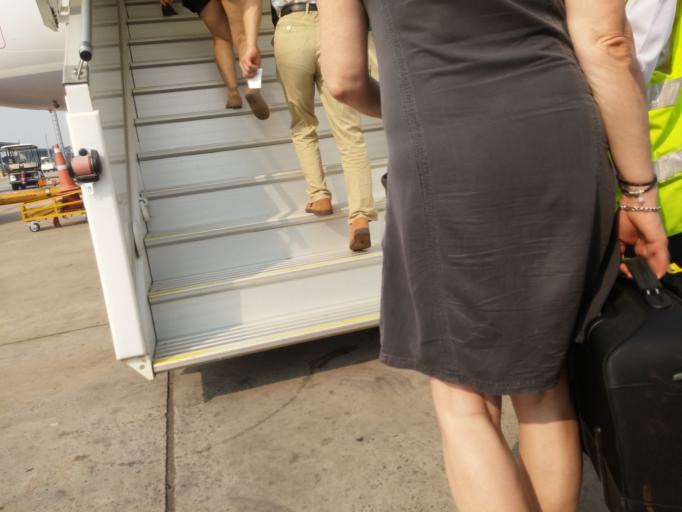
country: KH
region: Siem Reap
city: Siem Reap
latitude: 13.4083
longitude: 103.8140
